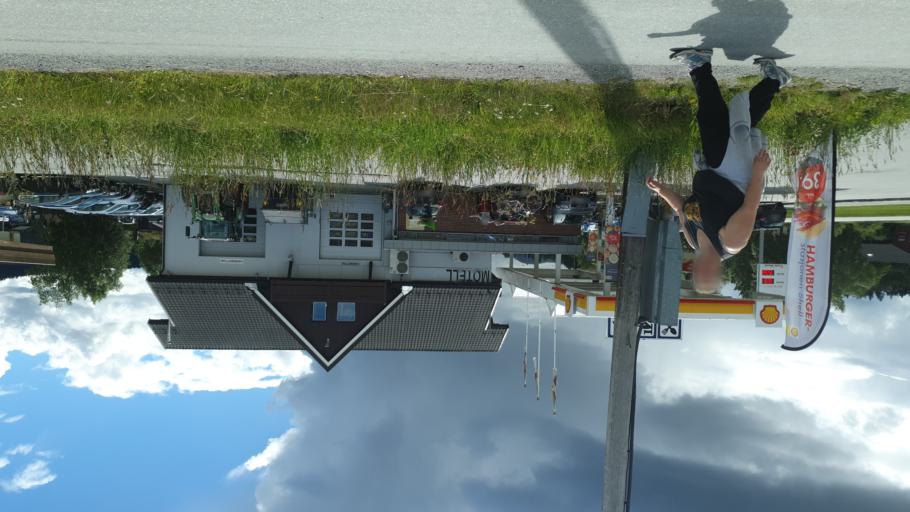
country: NO
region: Sor-Trondelag
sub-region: Rennebu
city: Berkak
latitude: 62.8324
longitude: 10.0112
